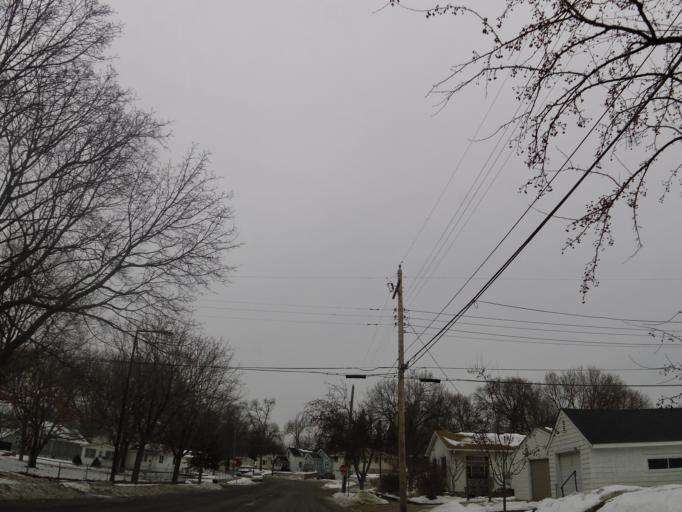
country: US
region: Minnesota
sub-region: Ramsey County
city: Maplewood
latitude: 44.9657
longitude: -93.0154
